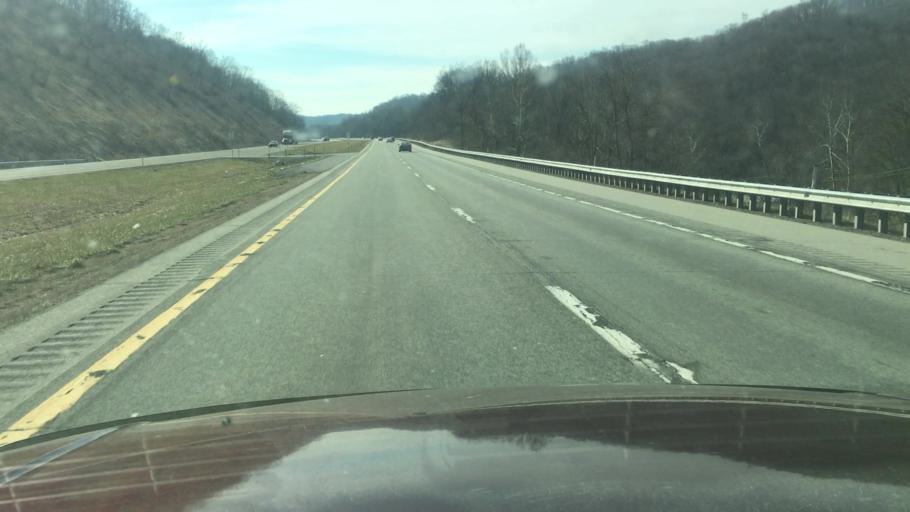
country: US
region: West Virginia
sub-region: Monongalia County
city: Star City
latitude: 39.7560
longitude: -80.0802
